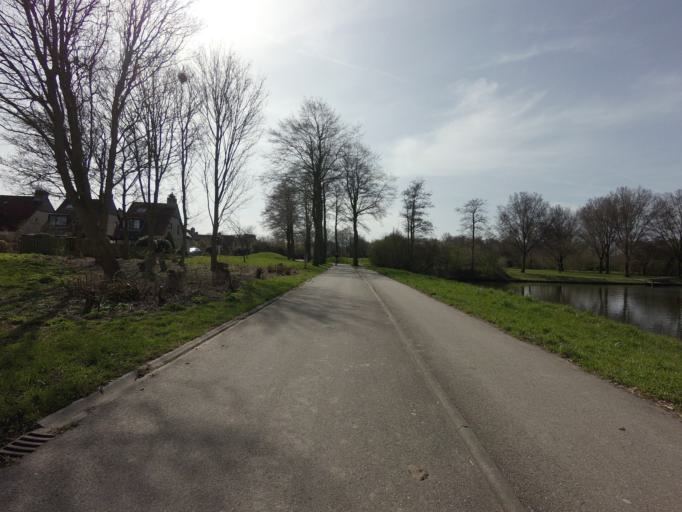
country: NL
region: South Holland
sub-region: Gemeente Zoetermeer
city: Zoetermeer
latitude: 52.0756
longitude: 4.5103
